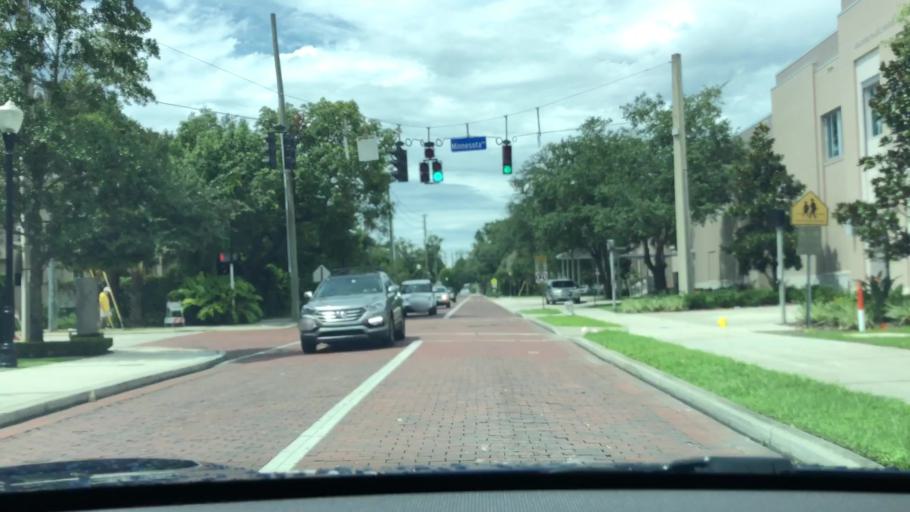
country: US
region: Florida
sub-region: Orange County
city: Winter Park
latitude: 28.5892
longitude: -81.3567
